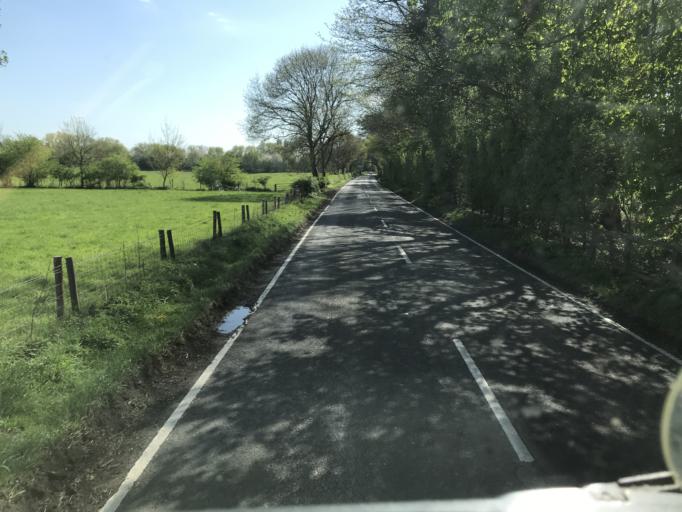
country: GB
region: England
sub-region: Cheshire East
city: Nantwich
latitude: 53.0818
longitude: -2.5225
